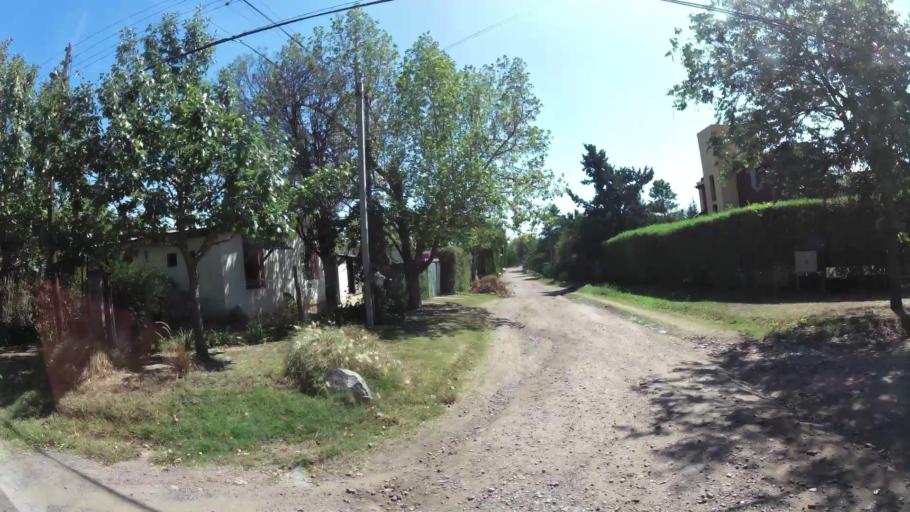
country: AR
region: Cordoba
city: Villa Allende
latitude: -31.2976
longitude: -64.2811
